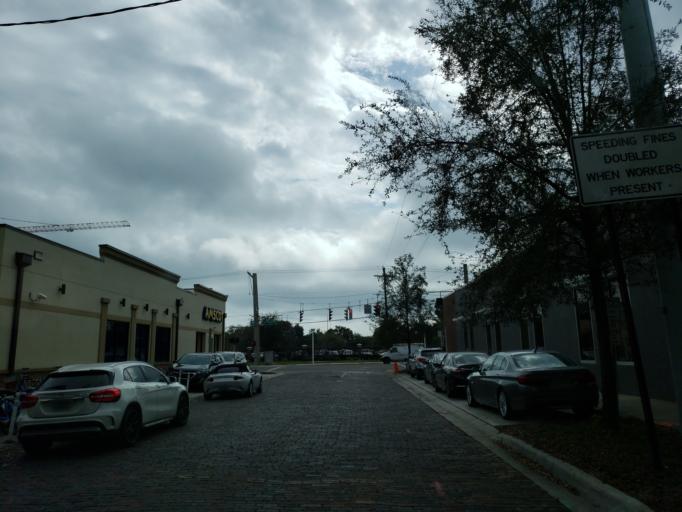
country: US
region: Florida
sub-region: Hillsborough County
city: Tampa
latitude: 27.9451
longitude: -82.4667
